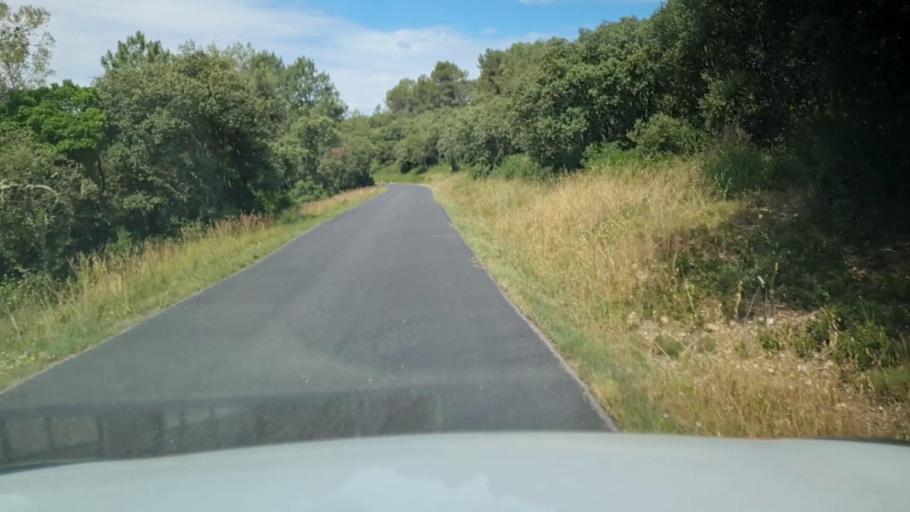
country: FR
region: Languedoc-Roussillon
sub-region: Departement du Gard
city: Calvisson
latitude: 43.8263
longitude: 4.1624
